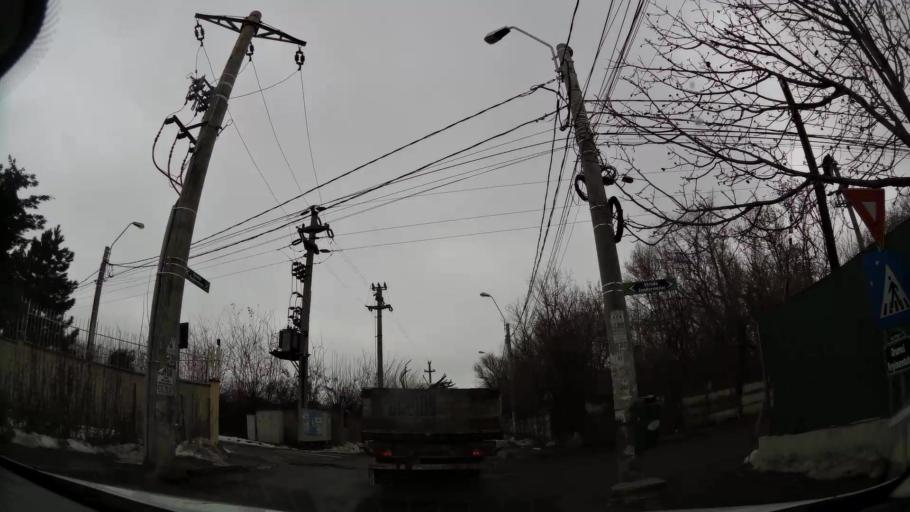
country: RO
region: Ilfov
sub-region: Comuna Otopeni
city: Otopeni
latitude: 44.5058
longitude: 26.0495
